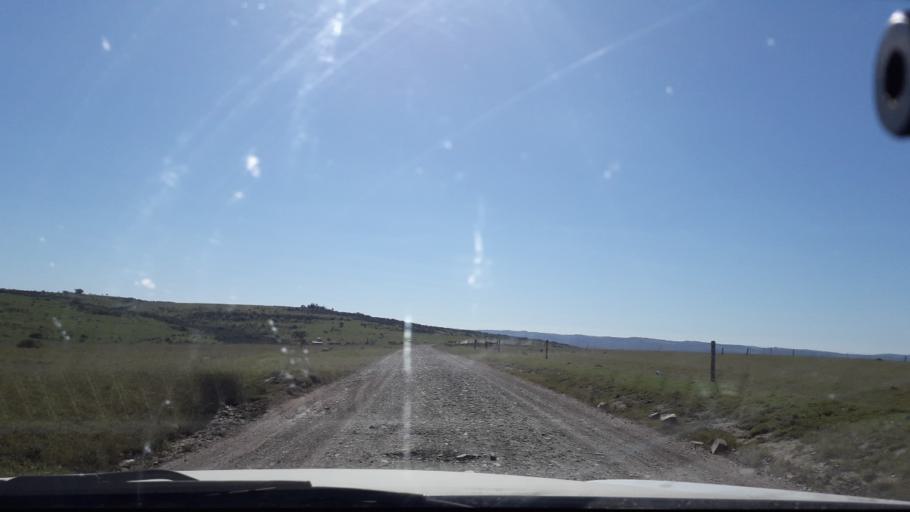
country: ZA
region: Eastern Cape
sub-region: Buffalo City Metropolitan Municipality
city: East London
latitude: -32.7971
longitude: 27.9512
